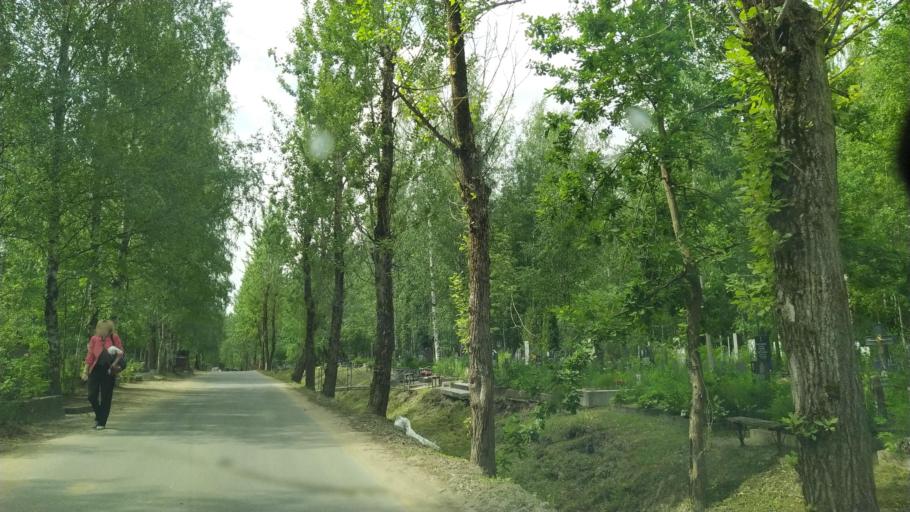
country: RU
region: St.-Petersburg
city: Dachnoye
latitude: 59.7665
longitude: 30.2624
